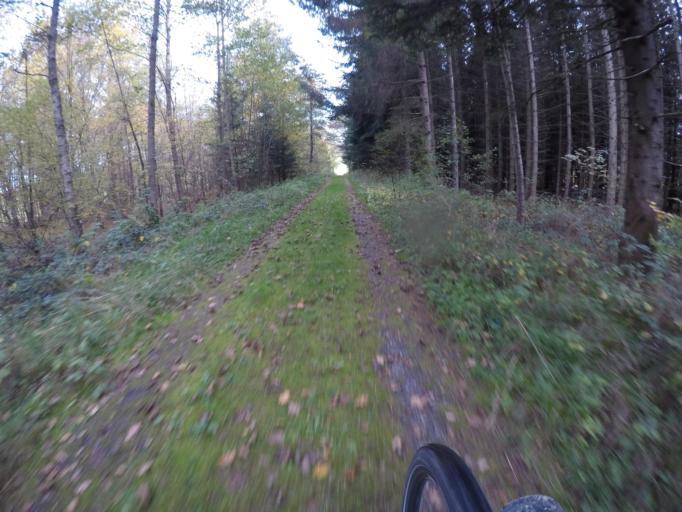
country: DE
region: Baden-Wuerttemberg
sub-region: Karlsruhe Region
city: Simmozheim
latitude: 48.7688
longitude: 8.7893
